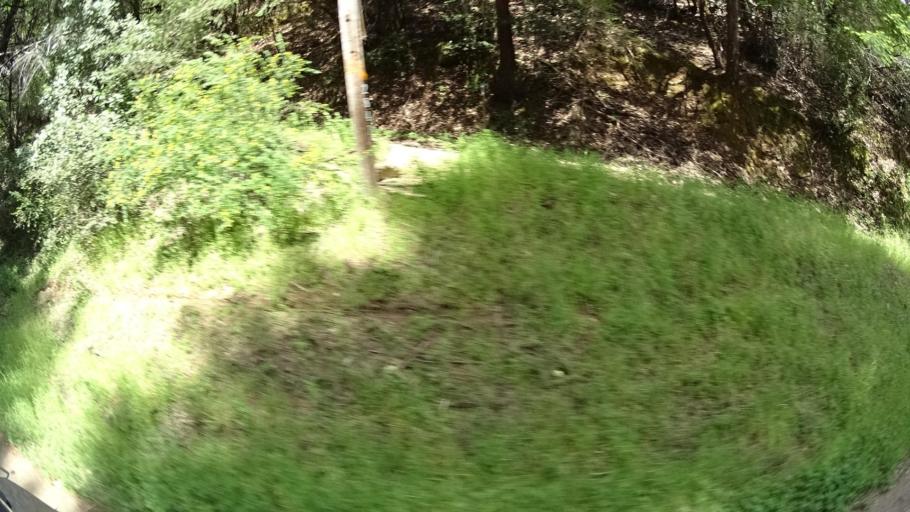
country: US
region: California
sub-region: Humboldt County
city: Redway
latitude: 40.0795
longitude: -123.8177
